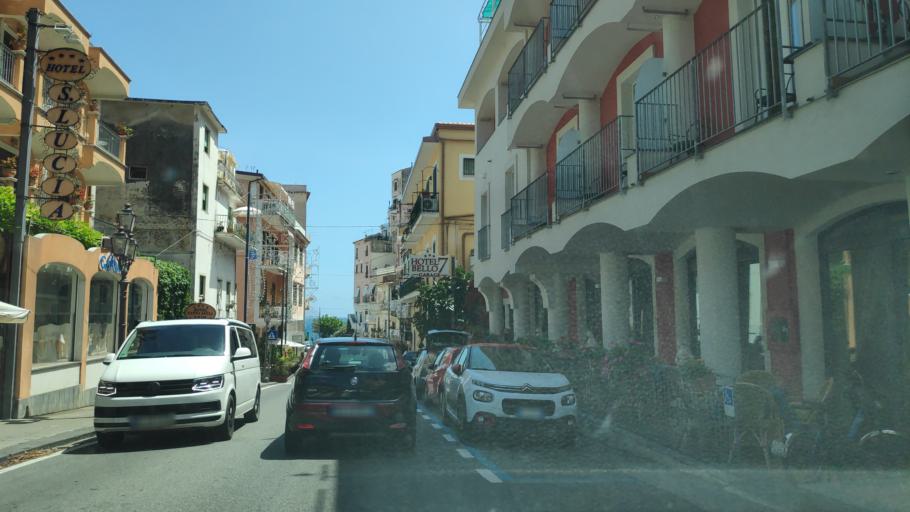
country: IT
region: Campania
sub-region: Provincia di Salerno
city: Minori
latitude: 40.6504
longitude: 14.6257
